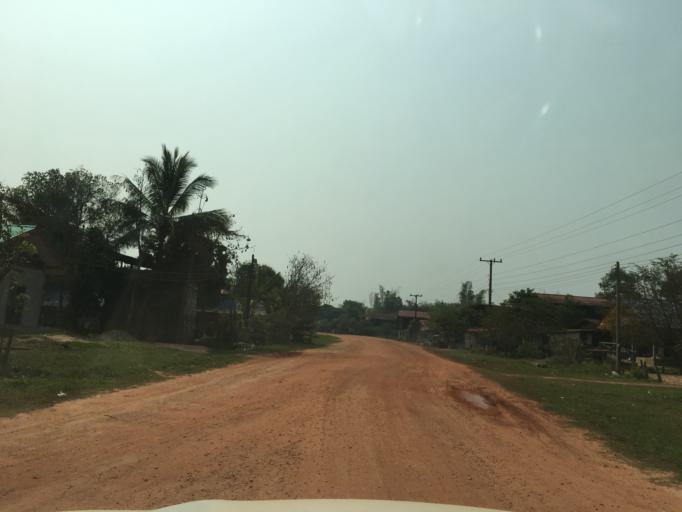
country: TH
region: Changwat Bueng Kan
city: Bung Khla
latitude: 18.2406
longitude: 104.0573
